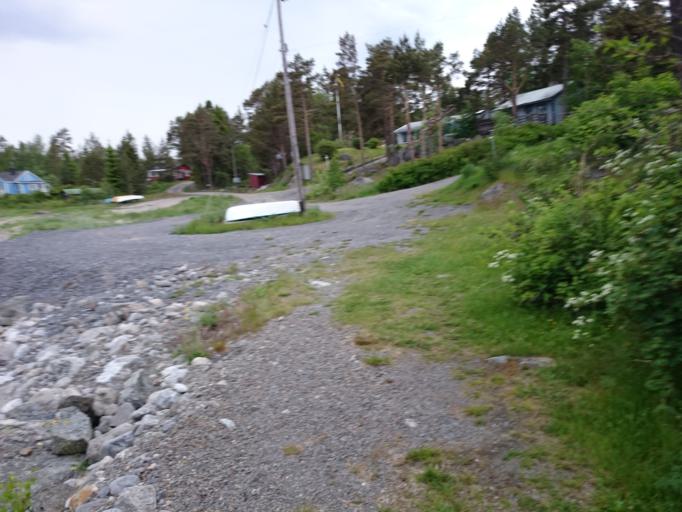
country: SE
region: Vaesternorrland
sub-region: Haernoesands Kommun
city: Haernoesand
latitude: 62.5852
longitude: 18.0079
